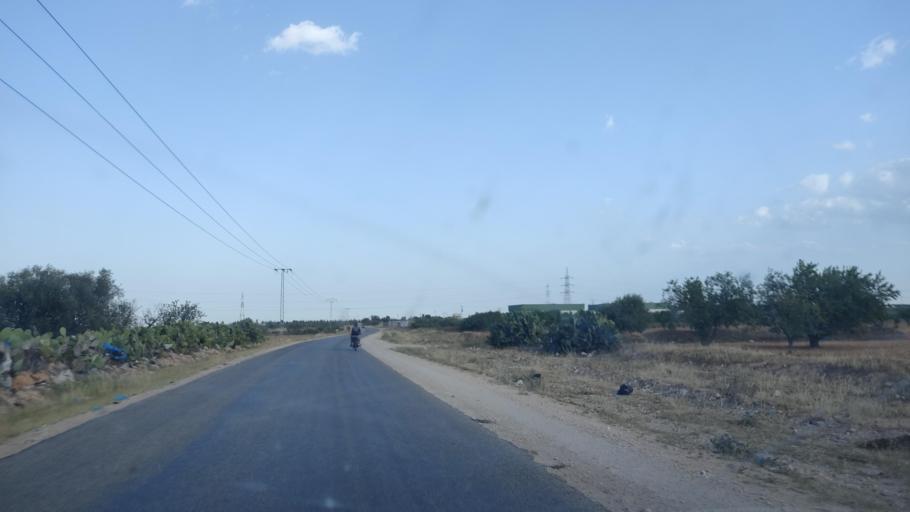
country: TN
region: Safaqis
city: Sfax
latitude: 34.8358
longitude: 10.6305
